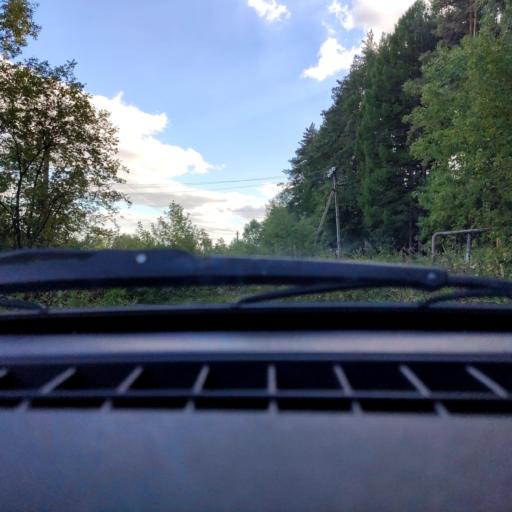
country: RU
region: Bashkortostan
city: Ufa
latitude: 54.8157
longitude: 56.1474
